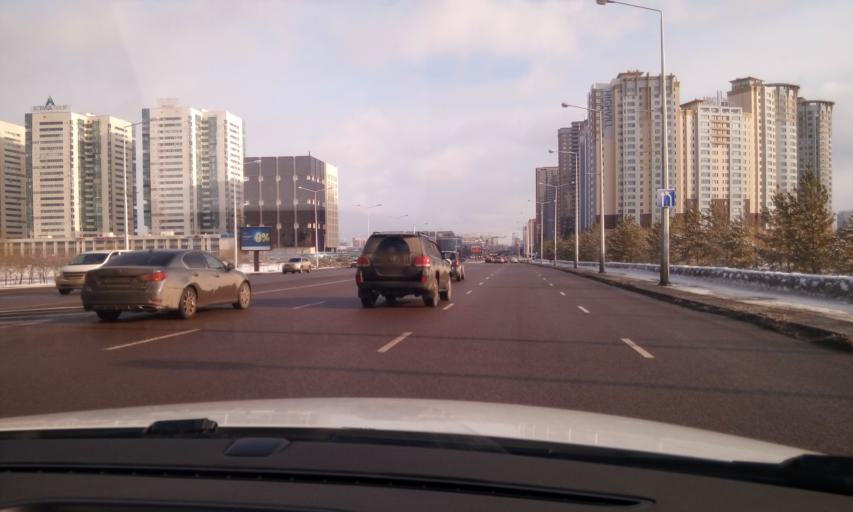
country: KZ
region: Astana Qalasy
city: Astana
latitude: 51.1301
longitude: 71.4539
